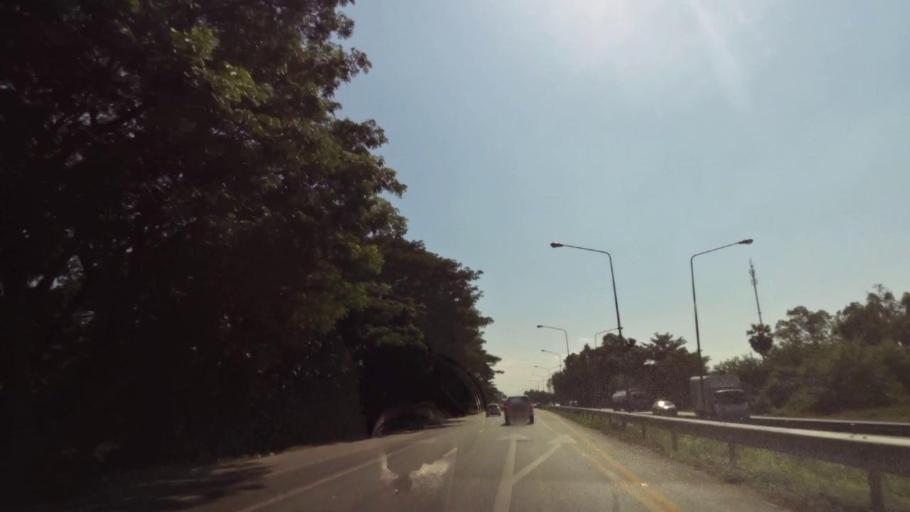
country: TH
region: Nakhon Sawan
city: Kao Liao
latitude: 15.7833
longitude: 100.1211
